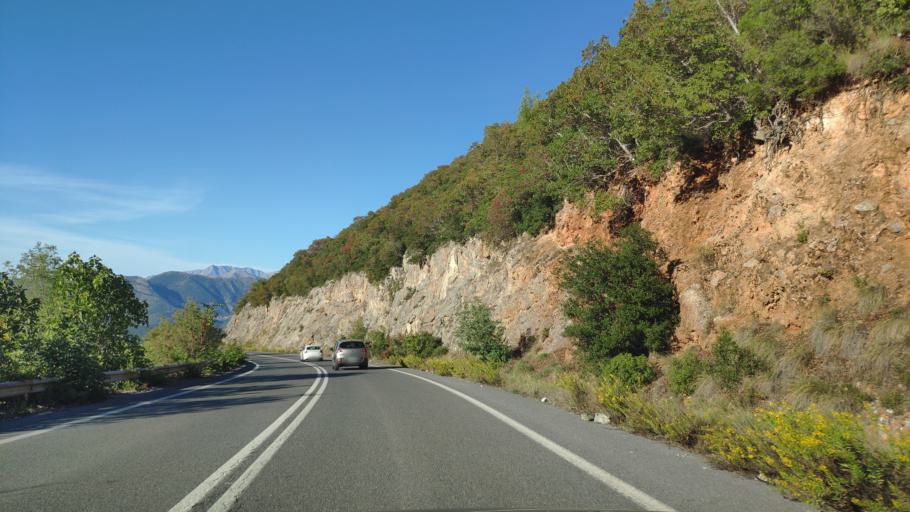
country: GR
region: Peloponnese
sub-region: Nomos Arkadias
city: Langadhia
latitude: 37.7207
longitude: 22.2024
